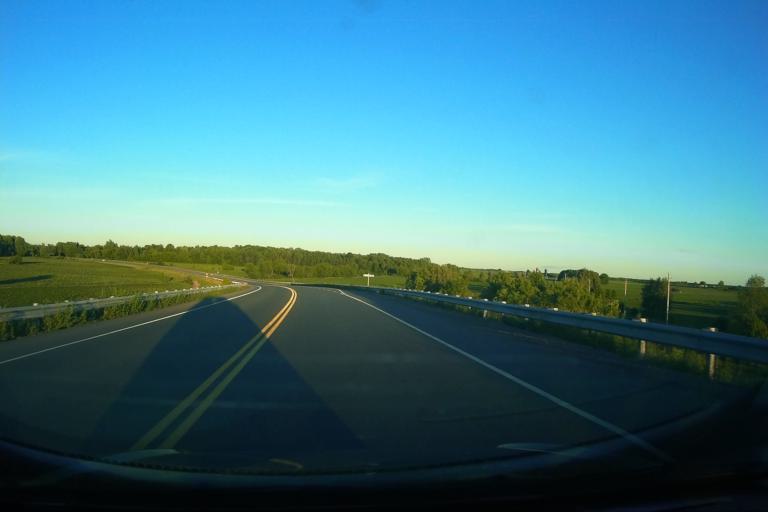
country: CA
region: Ontario
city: Casselman
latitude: 45.0738
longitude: -75.3642
